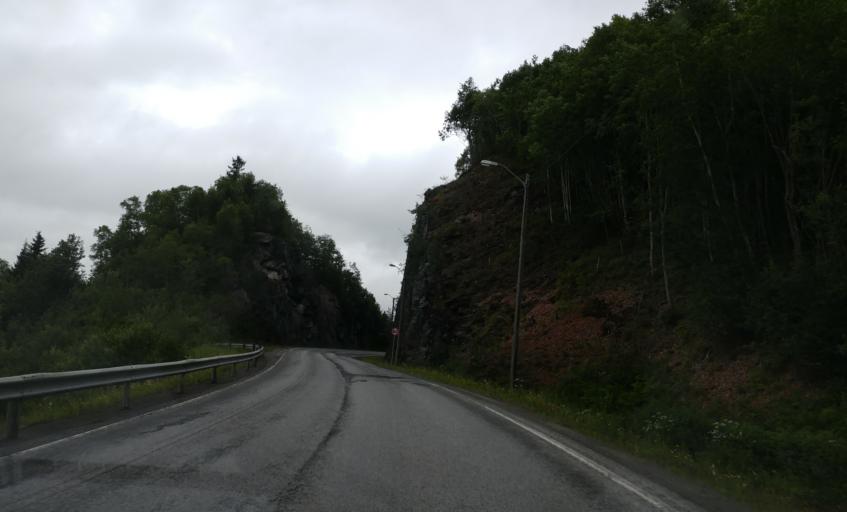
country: NO
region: Sor-Trondelag
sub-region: Selbu
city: Mebonden
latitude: 63.2410
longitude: 11.0572
